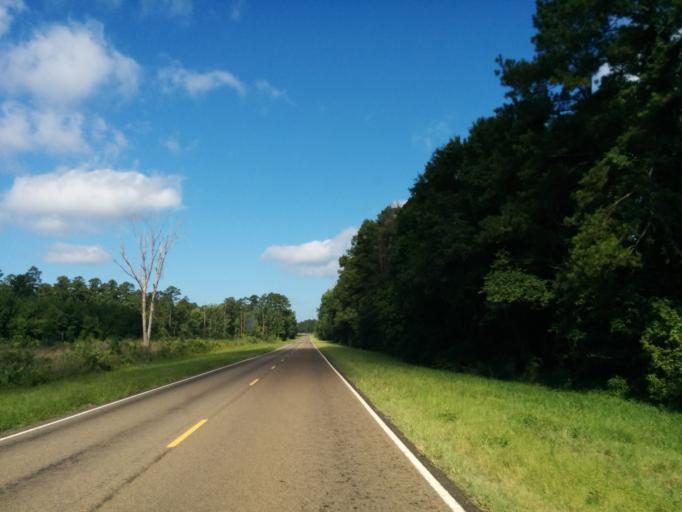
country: US
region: Texas
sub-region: San Augustine County
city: San Augustine
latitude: 31.4107
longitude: -94.0191
